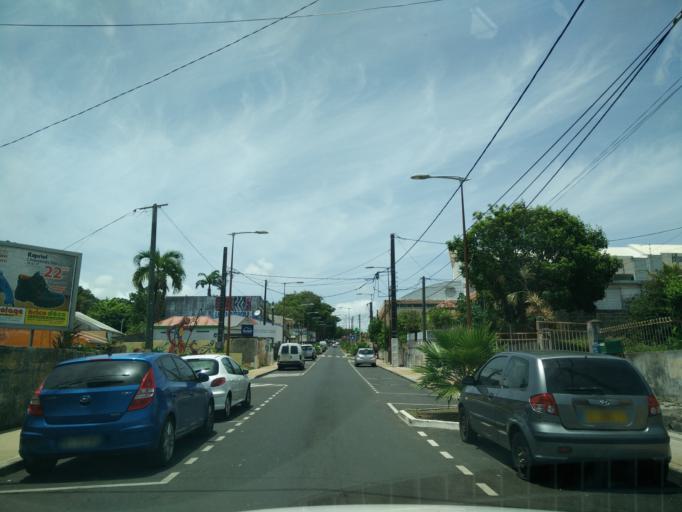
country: GP
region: Guadeloupe
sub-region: Guadeloupe
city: Petit-Bourg
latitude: 16.1937
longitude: -61.5927
